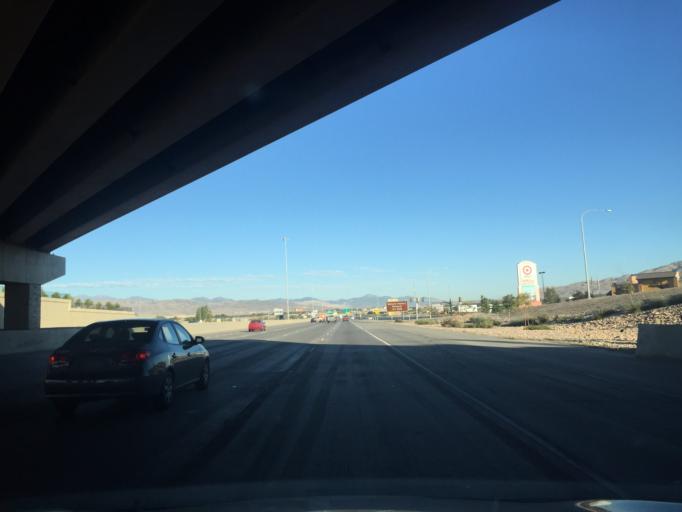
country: US
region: Utah
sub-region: Utah County
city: American Fork
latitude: 40.3769
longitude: -111.8185
